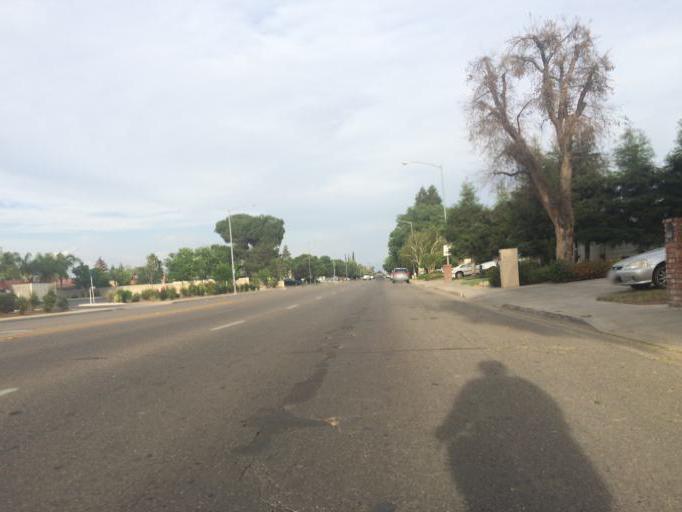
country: US
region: California
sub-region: Fresno County
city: Clovis
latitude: 36.8157
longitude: -119.6904
